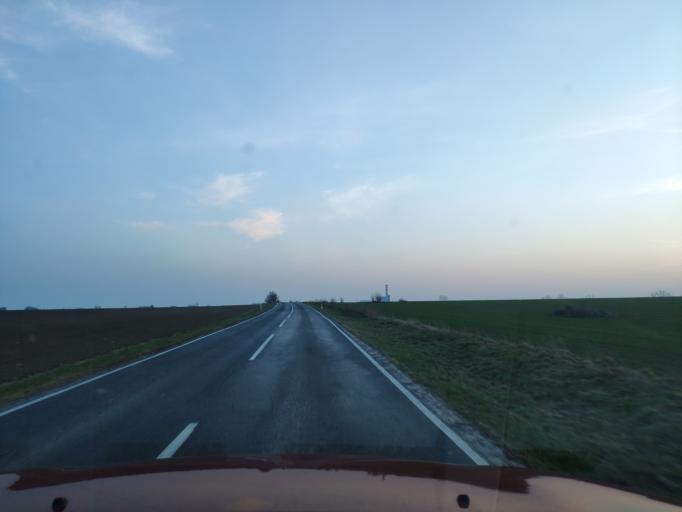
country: SK
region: Trnavsky
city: Leopoldov
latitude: 48.4733
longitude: 17.7066
